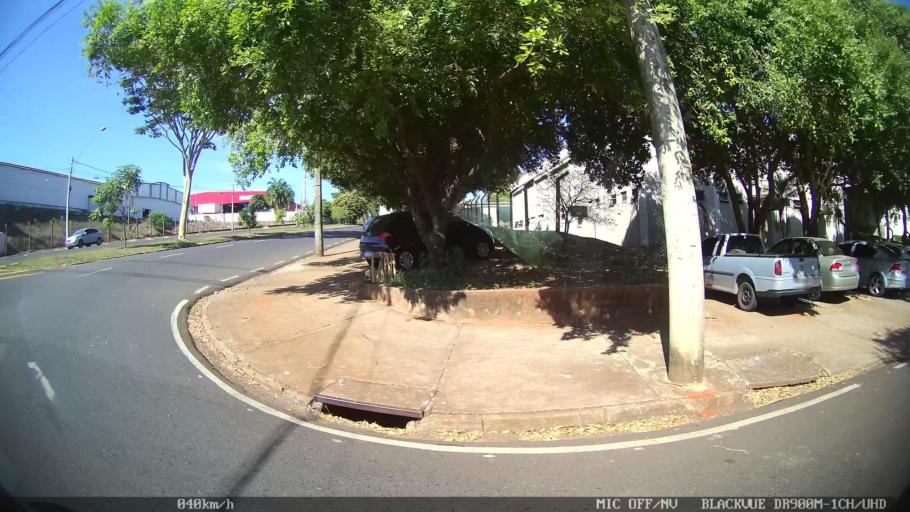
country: BR
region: Sao Paulo
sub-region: Sao Jose Do Rio Preto
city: Sao Jose do Rio Preto
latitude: -20.8109
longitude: -49.4149
